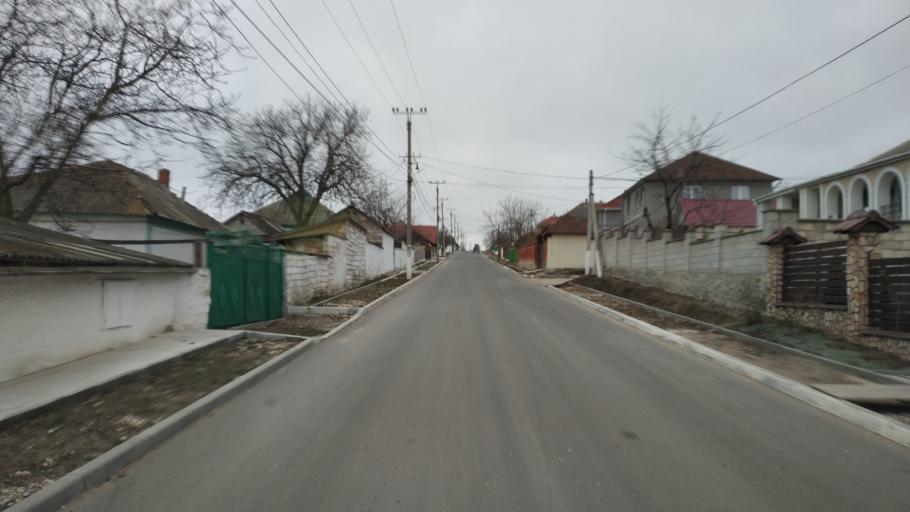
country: MD
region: Laloveni
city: Ialoveni
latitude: 46.9078
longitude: 28.8005
